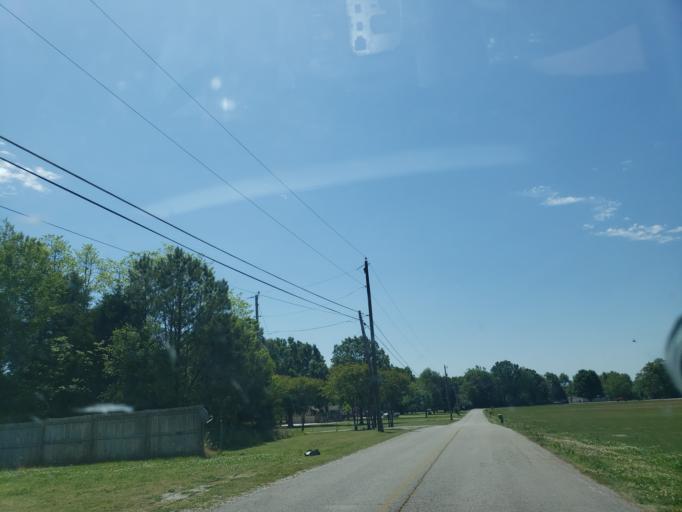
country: US
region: Alabama
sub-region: Madison County
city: Hazel Green
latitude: 34.9531
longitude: -86.5342
